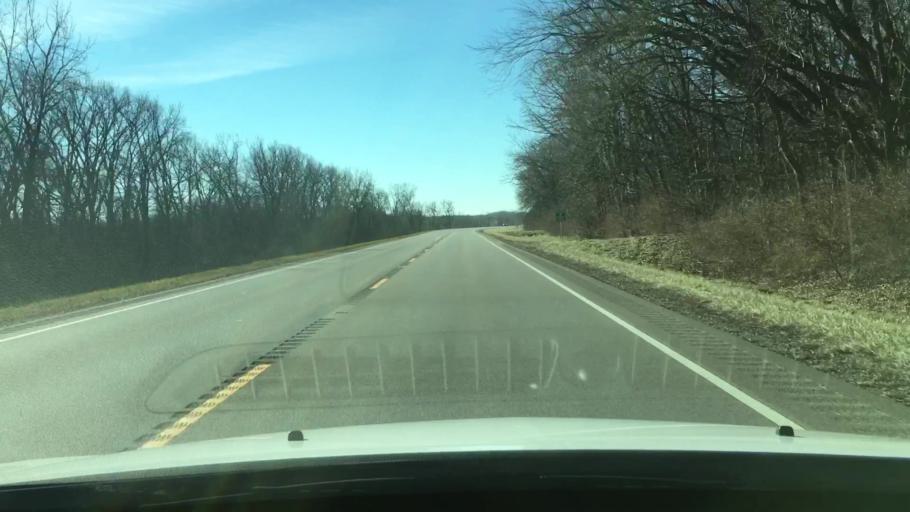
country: US
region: Illinois
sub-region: Peoria County
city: Glasford
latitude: 40.5269
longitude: -89.8778
